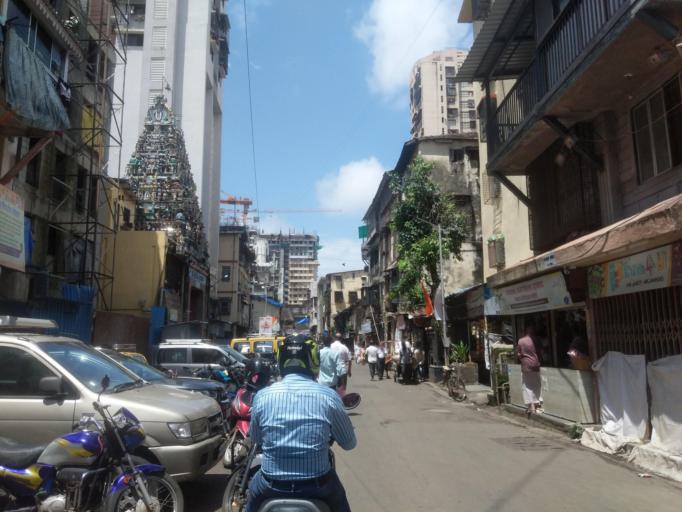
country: IN
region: Maharashtra
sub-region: Mumbai Suburban
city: Mumbai
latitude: 18.9516
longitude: 72.8257
